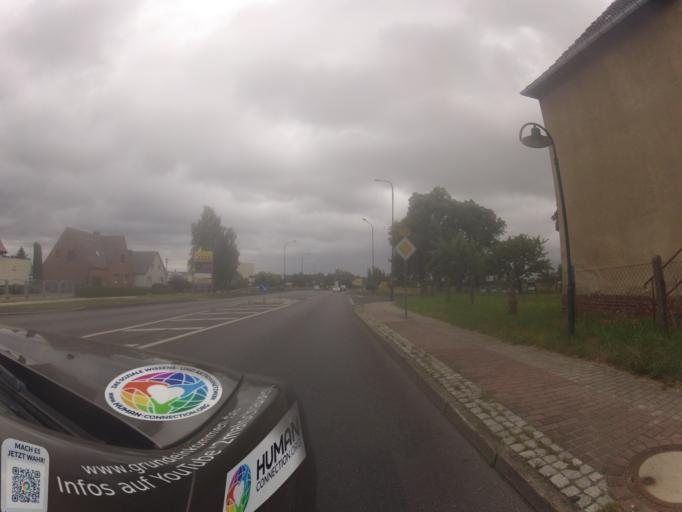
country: DE
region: Mecklenburg-Vorpommern
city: Pasewalk
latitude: 53.5178
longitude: 13.9778
